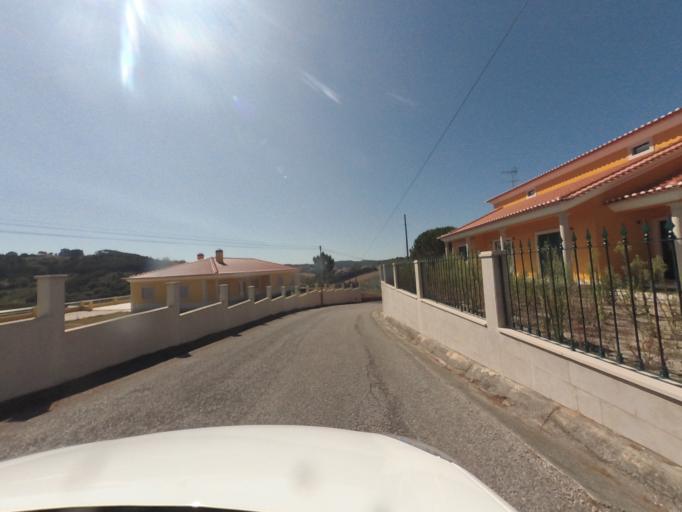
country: PT
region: Leiria
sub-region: Alcobaca
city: Turquel
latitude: 39.4855
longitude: -8.9916
